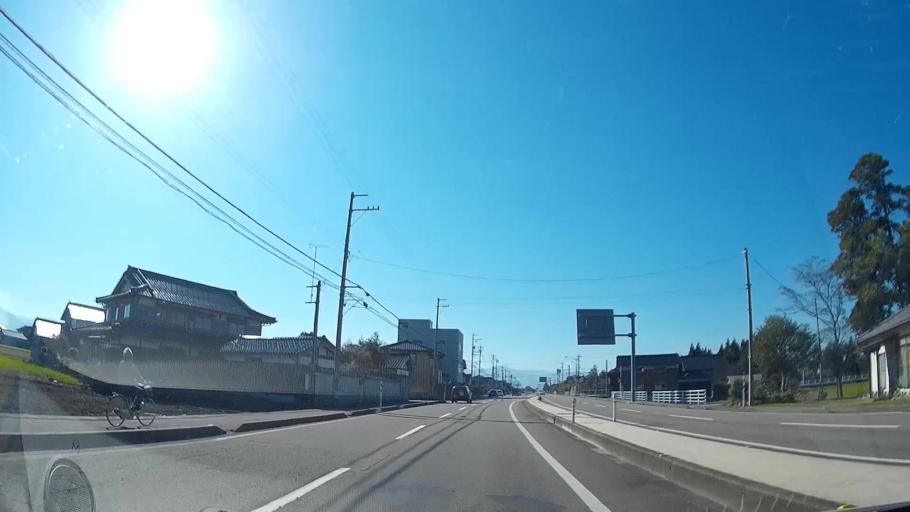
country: JP
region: Toyama
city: Nanto-shi
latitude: 36.6220
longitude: 136.9426
